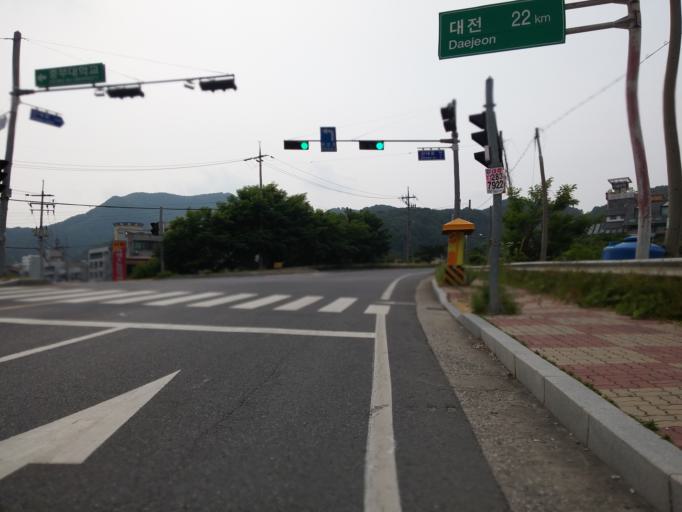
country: KR
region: Chungcheongnam-do
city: Kinzan
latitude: 36.1942
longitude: 127.4592
